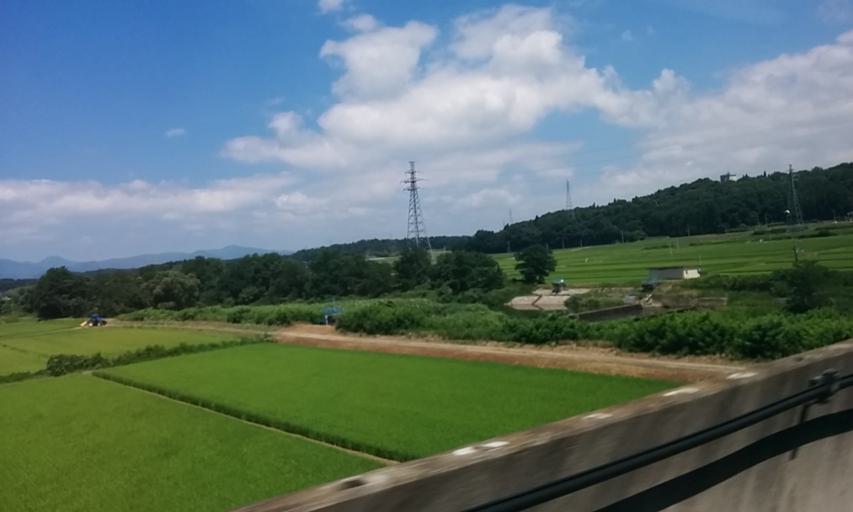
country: JP
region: Fukushima
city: Sukagawa
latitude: 37.2603
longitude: 140.3096
